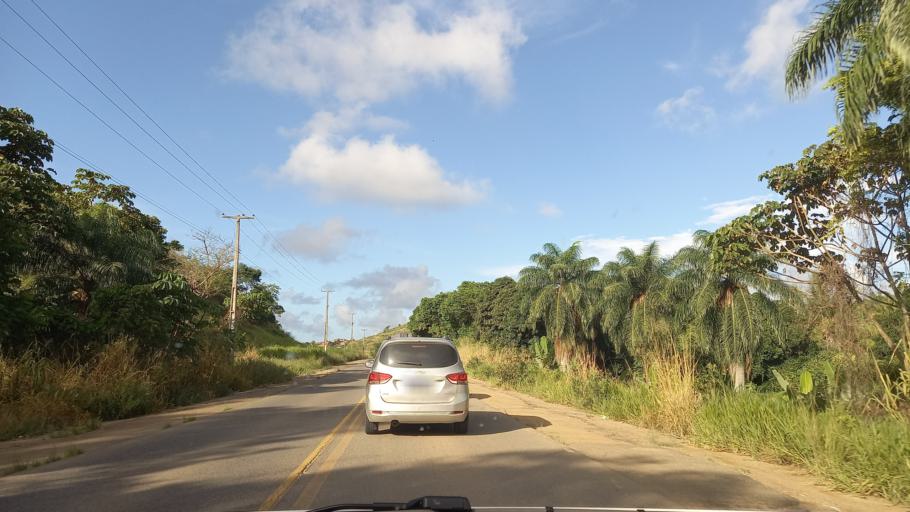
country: BR
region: Pernambuco
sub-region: Sirinhaem
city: Sirinhaem
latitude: -8.6191
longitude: -35.1239
